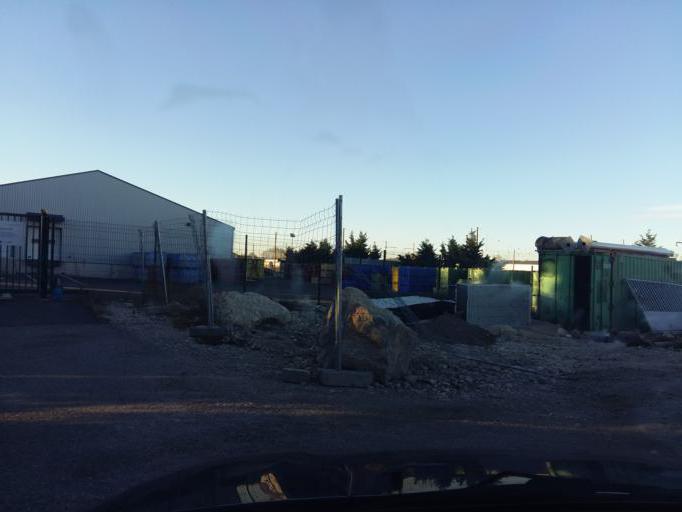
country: FR
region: Provence-Alpes-Cote d'Azur
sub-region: Departement du Vaucluse
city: Avignon
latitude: 43.9349
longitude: 4.8388
